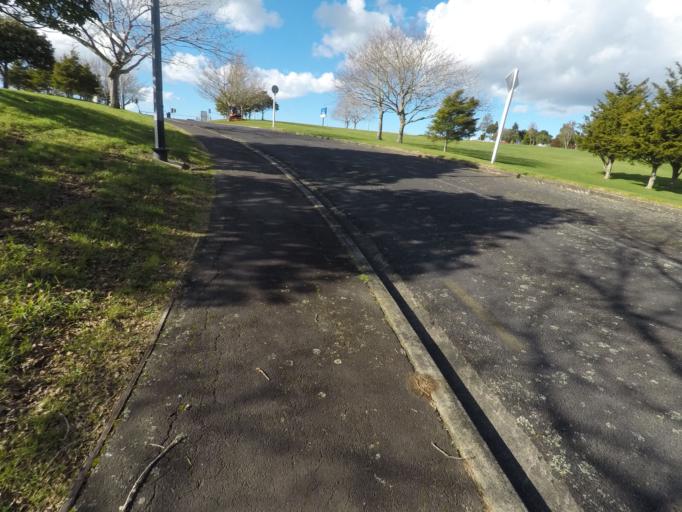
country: NZ
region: Auckland
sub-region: Auckland
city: Rothesay Bay
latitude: -36.7304
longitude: 174.7004
